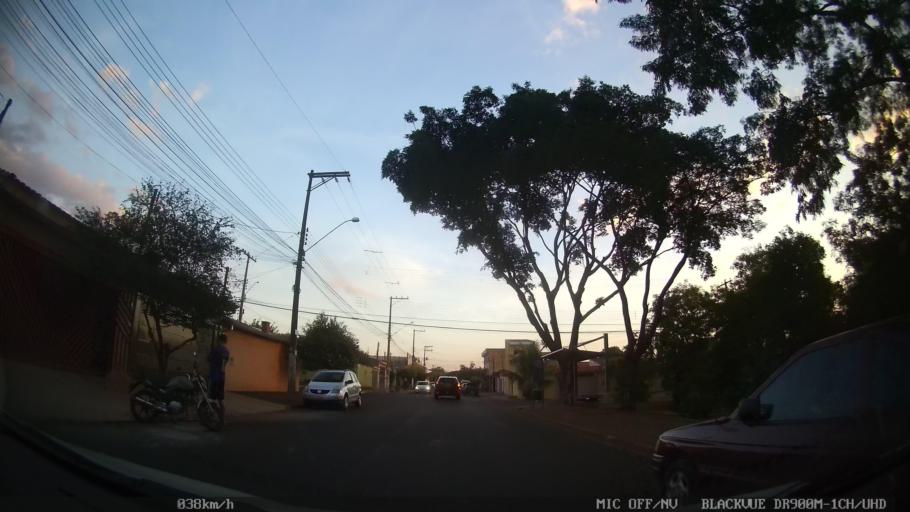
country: BR
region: Sao Paulo
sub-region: Ribeirao Preto
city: Ribeirao Preto
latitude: -21.1402
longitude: -47.8225
